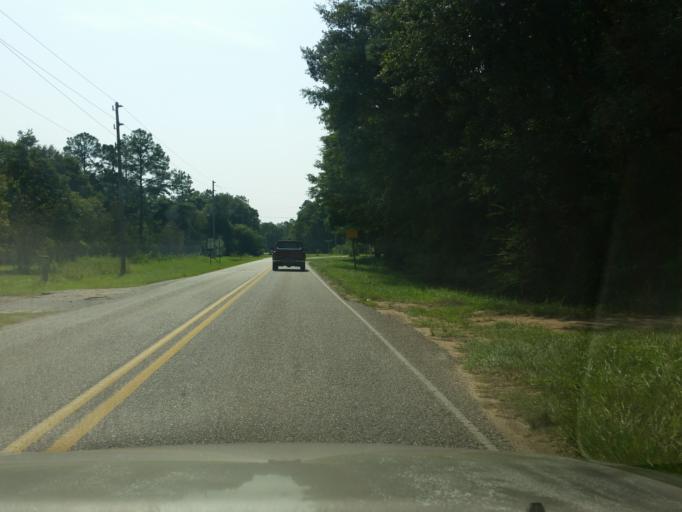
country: US
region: Alabama
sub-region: Baldwin County
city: Elberta
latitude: 30.5142
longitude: -87.4731
